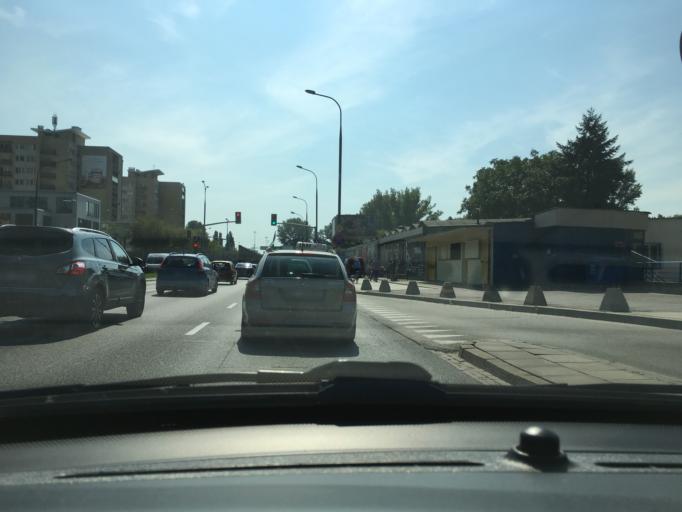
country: PL
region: Masovian Voivodeship
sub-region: Warszawa
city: Praga Polnoc
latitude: 52.2309
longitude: 21.0499
